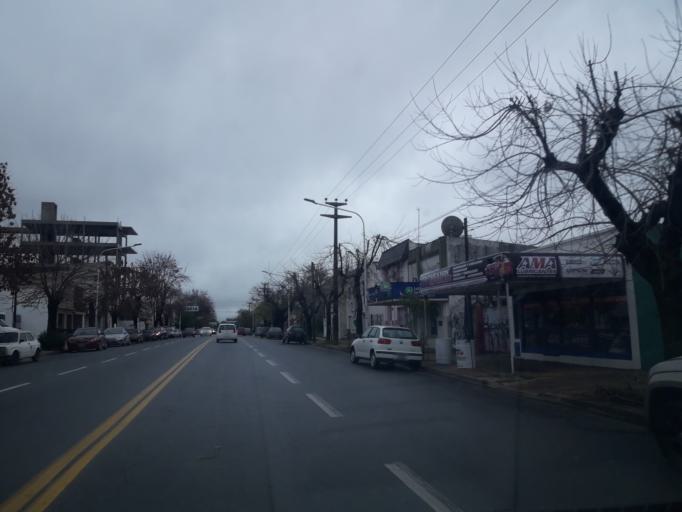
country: AR
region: Buenos Aires
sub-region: Partido de Tandil
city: Tandil
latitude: -37.3233
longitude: -59.1486
